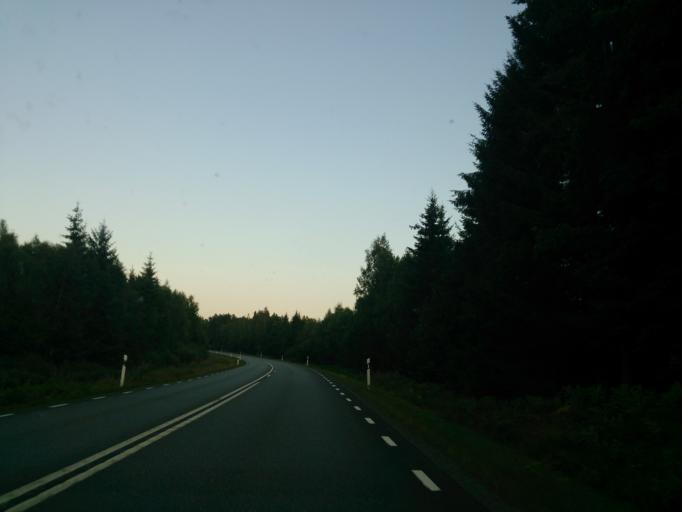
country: SE
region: Joenkoeping
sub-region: Varnamo Kommun
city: Bor
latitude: 57.0647
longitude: 14.1839
